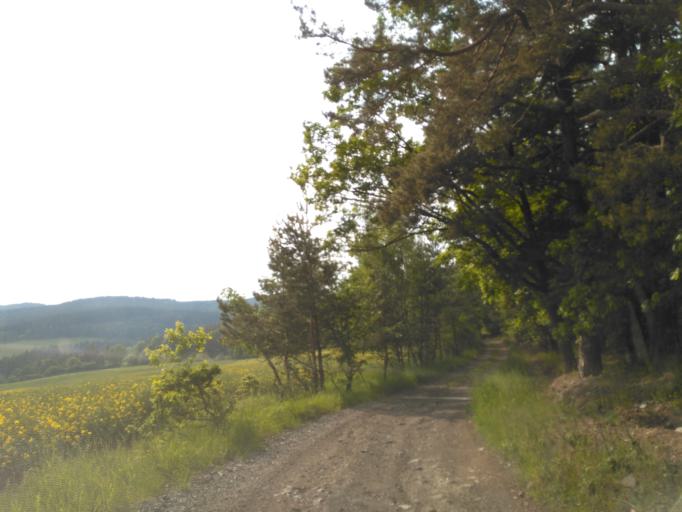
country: CZ
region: Plzensky
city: Zbiroh
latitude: 49.8588
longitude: 13.7374
